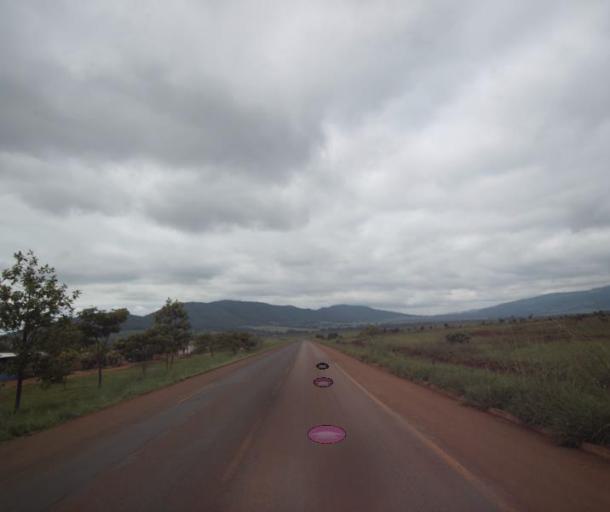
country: BR
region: Goias
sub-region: Barro Alto
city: Barro Alto
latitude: -14.9731
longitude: -48.9302
